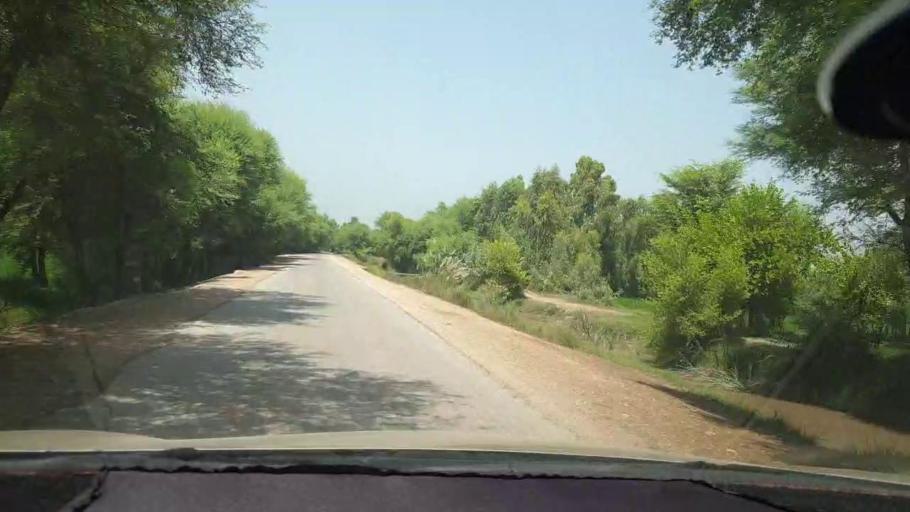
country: PK
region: Sindh
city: Kambar
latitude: 27.6543
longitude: 67.9626
